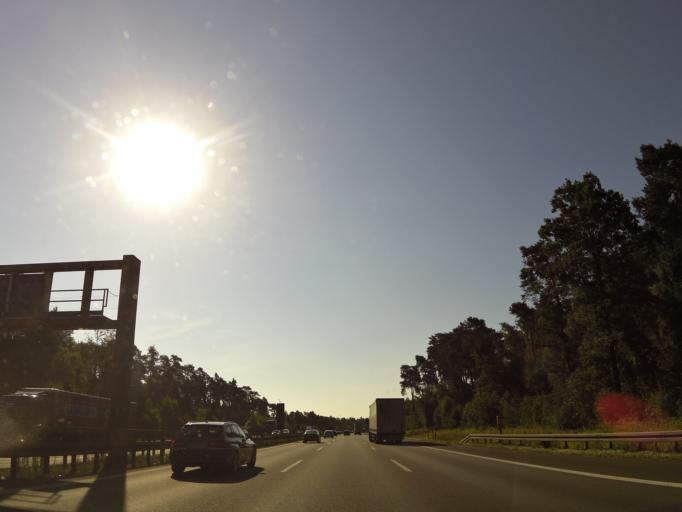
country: DE
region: Bavaria
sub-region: Regierungsbezirk Mittelfranken
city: Buckenhof
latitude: 49.5317
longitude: 11.0534
